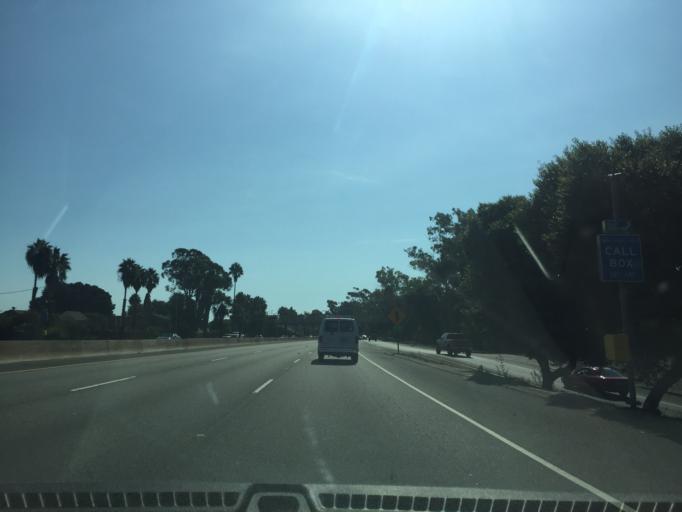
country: US
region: California
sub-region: Santa Barbara County
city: Santa Barbara
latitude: 34.4158
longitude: -119.7067
